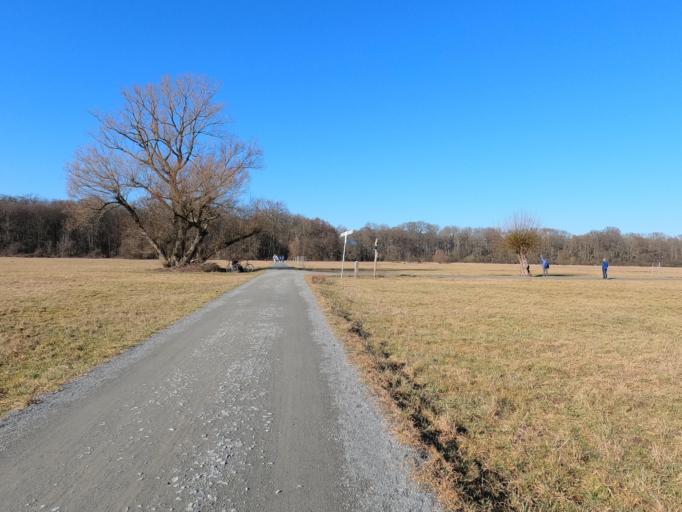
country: DE
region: Hesse
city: Kelsterbach
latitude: 50.0767
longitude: 8.5616
